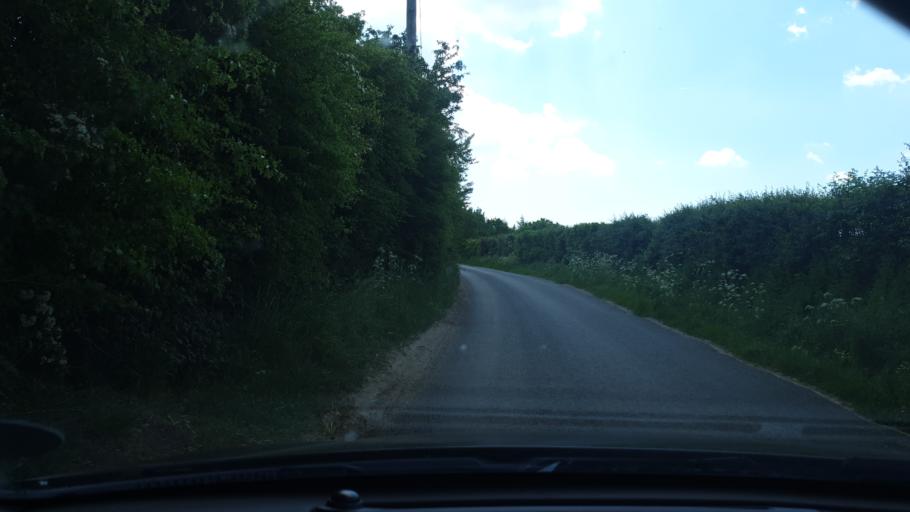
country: GB
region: England
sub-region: Essex
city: Great Bentley
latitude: 51.8428
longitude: 1.0909
